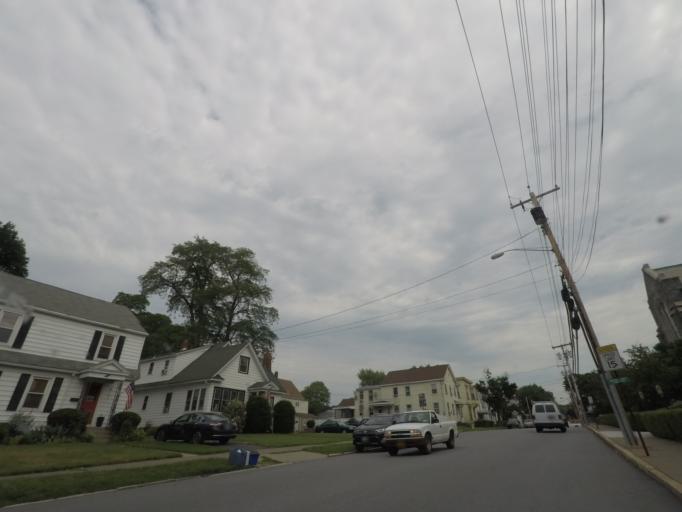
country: US
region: New York
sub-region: Saratoga County
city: Waterford
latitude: 42.7913
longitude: -73.6815
